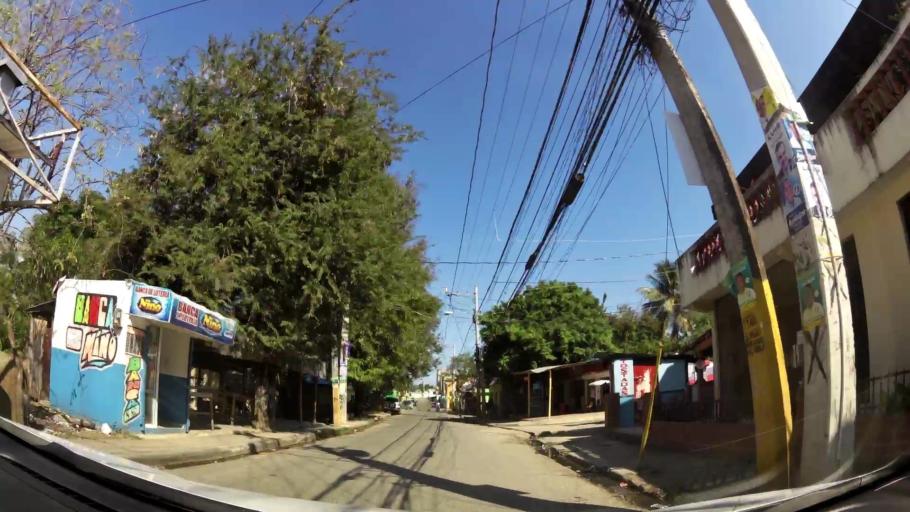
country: DO
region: Santo Domingo
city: Santo Domingo Oeste
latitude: 18.4720
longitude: -70.0033
